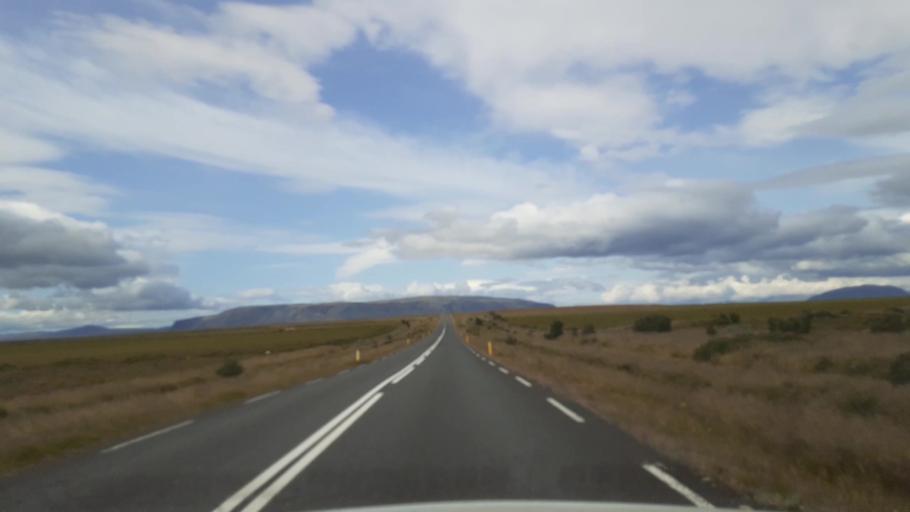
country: IS
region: South
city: Selfoss
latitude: 63.9139
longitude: -20.8354
